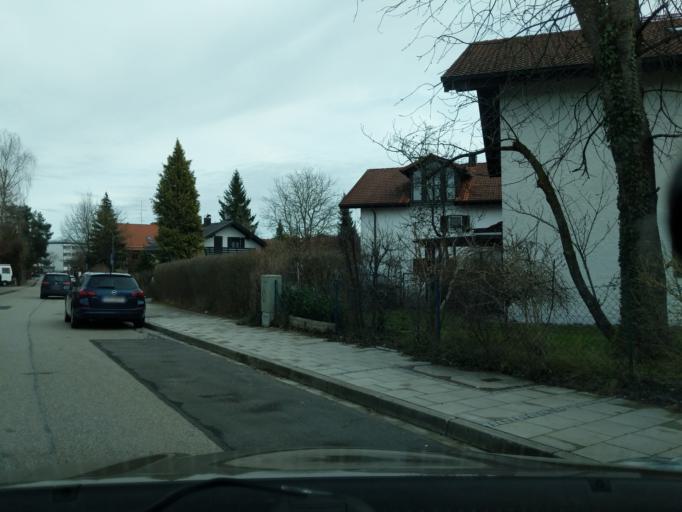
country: DE
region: Bavaria
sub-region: Upper Bavaria
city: Zorneding
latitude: 48.0855
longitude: 11.8257
